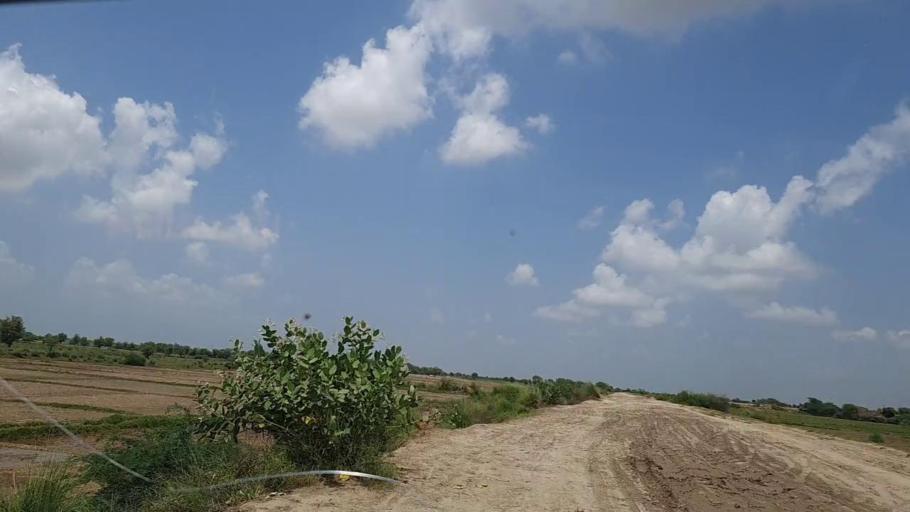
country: PK
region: Sindh
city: Tharu Shah
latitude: 26.9437
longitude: 68.0136
